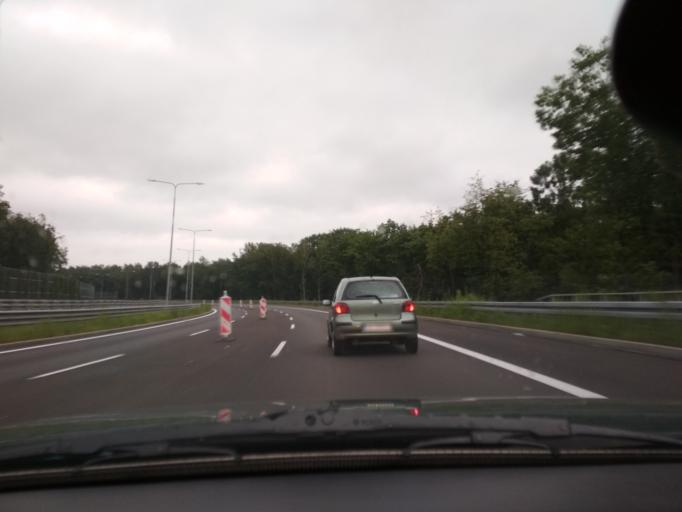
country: PL
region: Silesian Voivodeship
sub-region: Powiat gliwicki
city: Przyszowice
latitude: 50.2852
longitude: 18.7653
